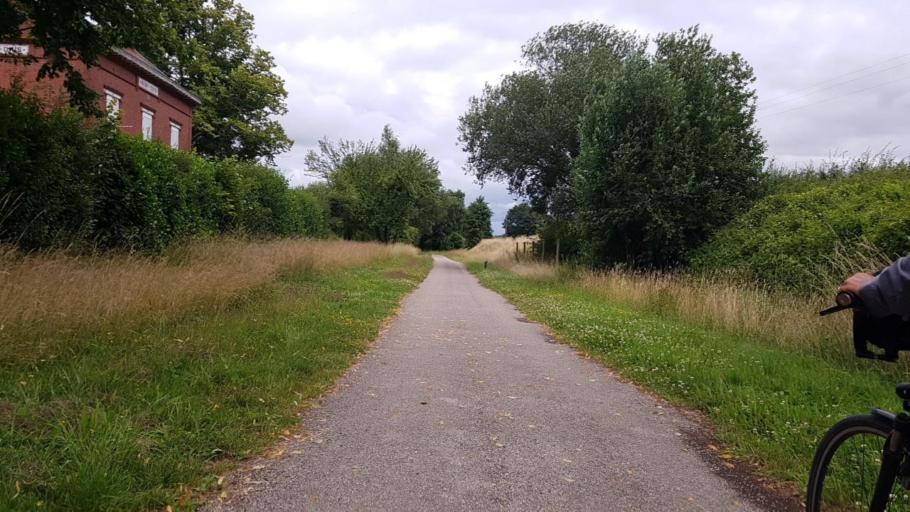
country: FR
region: Picardie
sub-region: Departement de l'Aisne
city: Origny-en-Thierache
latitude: 49.9318
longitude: 4.0010
